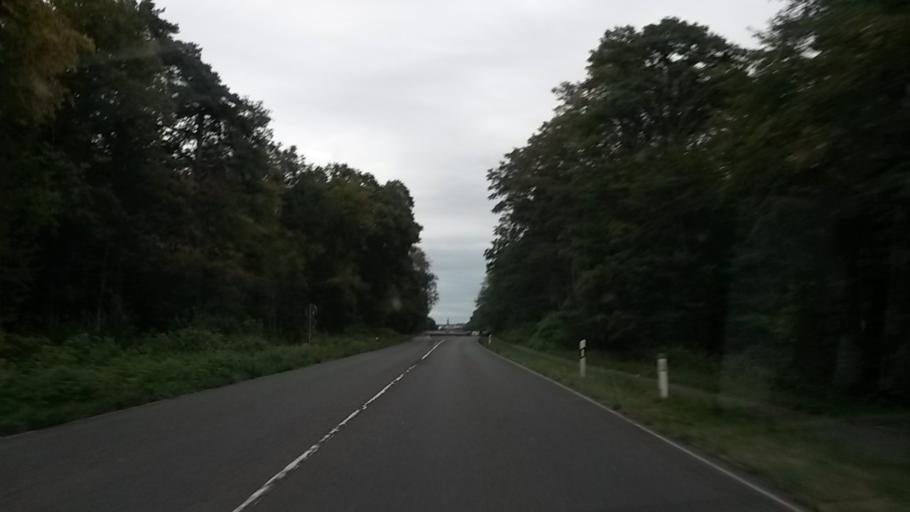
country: DE
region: North Rhine-Westphalia
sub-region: Regierungsbezirk Koln
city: Rath
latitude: 50.9458
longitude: 7.1210
